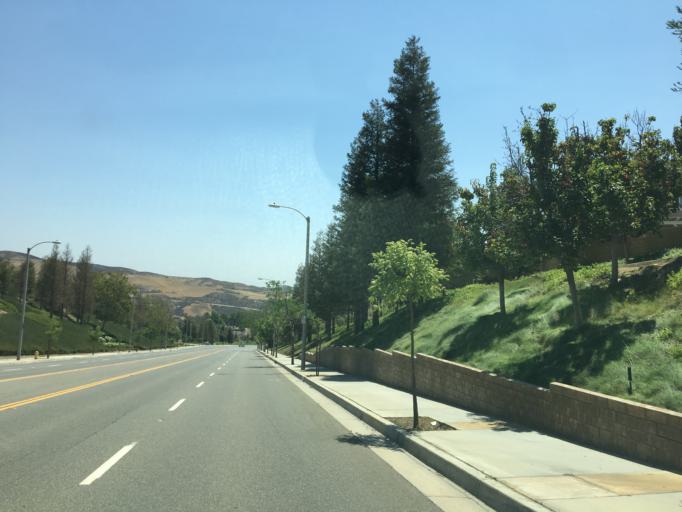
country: US
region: California
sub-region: Los Angeles County
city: Castaic
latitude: 34.5038
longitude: -118.6213
